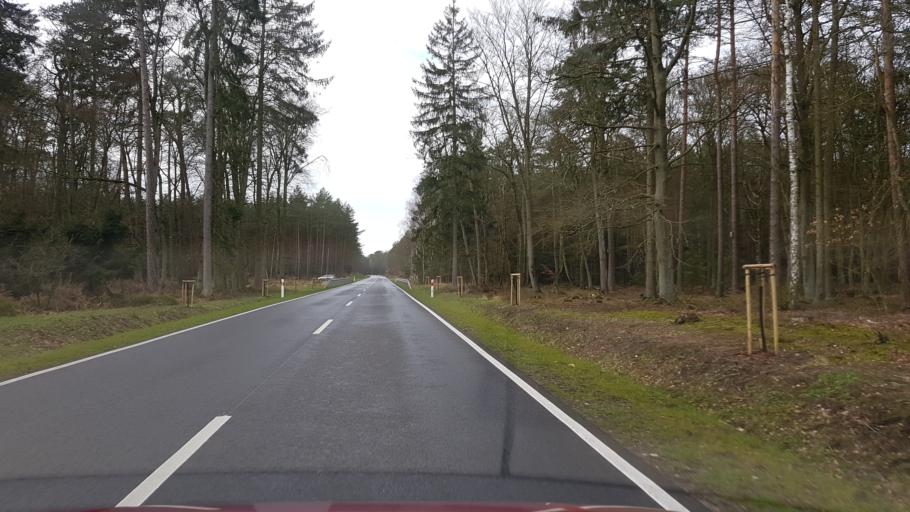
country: PL
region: West Pomeranian Voivodeship
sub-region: Powiat policki
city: Nowe Warpno
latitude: 53.6669
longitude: 14.4311
